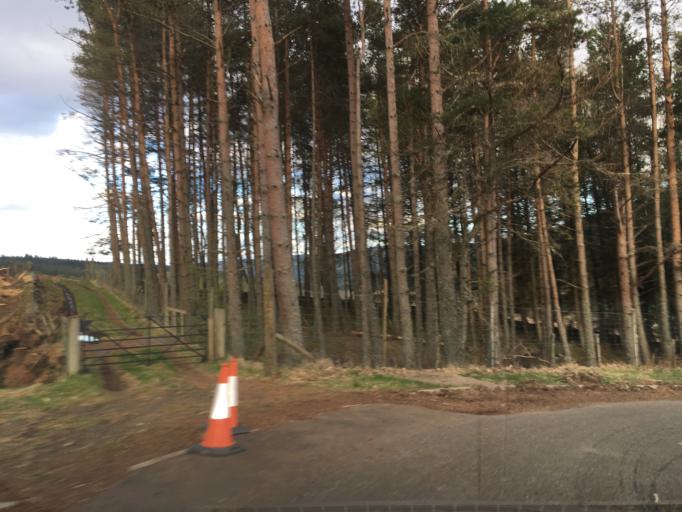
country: GB
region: Scotland
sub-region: Perth and Kinross
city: Aberfeldy
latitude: 56.7602
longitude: -4.0800
